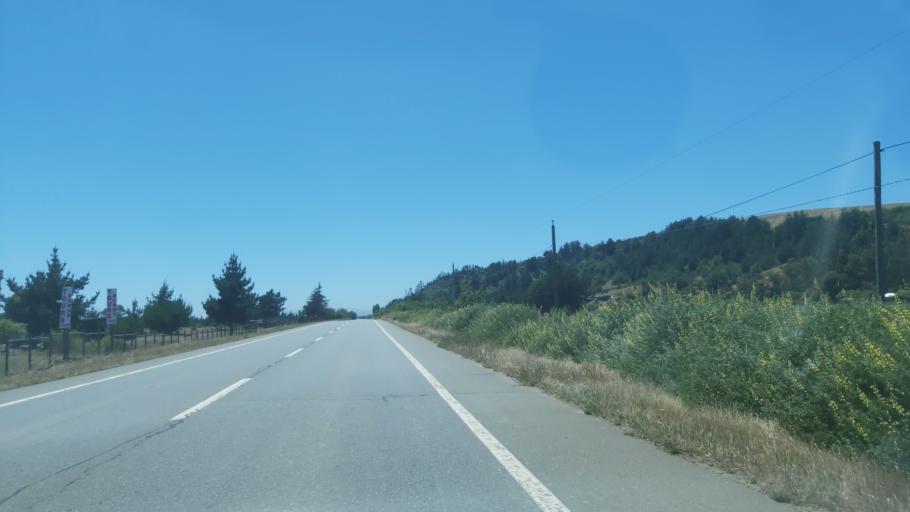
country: CL
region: Maule
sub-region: Provincia de Talca
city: Constitucion
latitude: -35.1687
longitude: -72.2645
